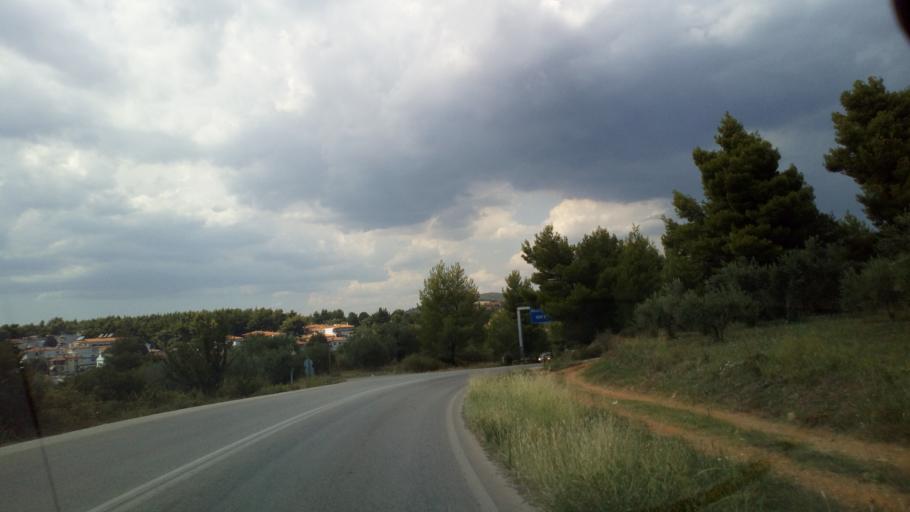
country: GR
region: Central Macedonia
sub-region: Nomos Chalkidikis
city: Nikiti
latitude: 40.2298
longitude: 23.6082
